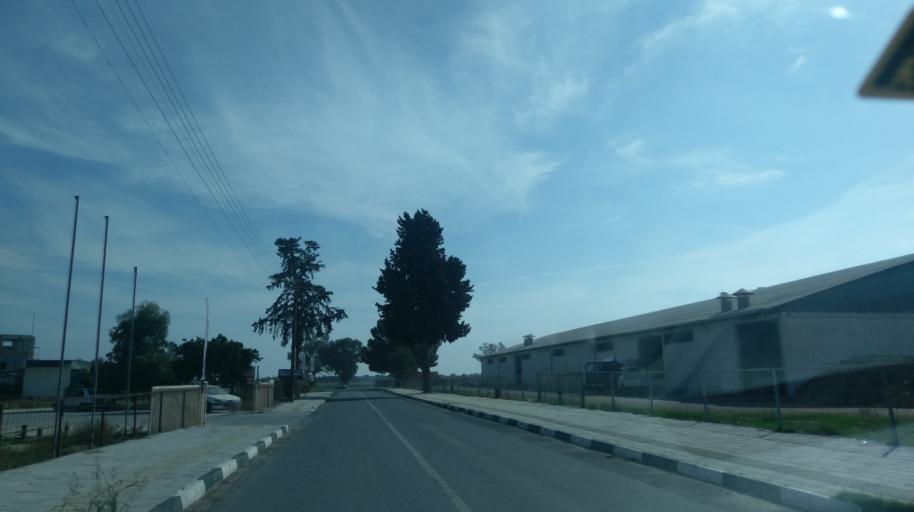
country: CY
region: Larnaka
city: Pergamos
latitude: 35.1065
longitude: 33.6915
